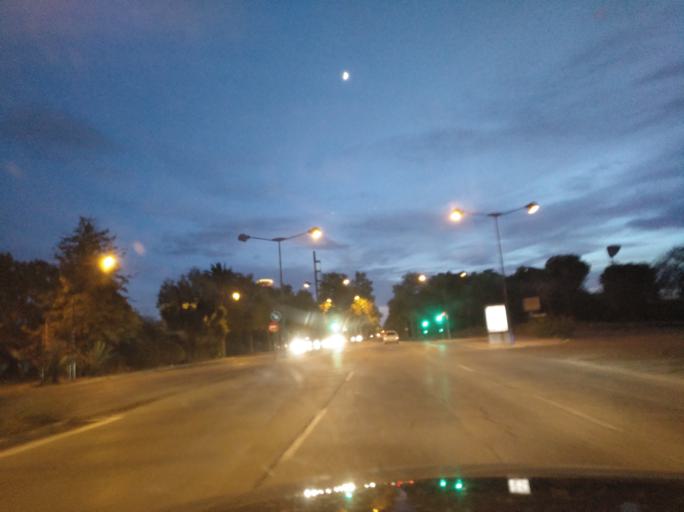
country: ES
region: Andalusia
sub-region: Provincia de Sevilla
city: Camas
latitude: 37.4042
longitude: -6.0104
